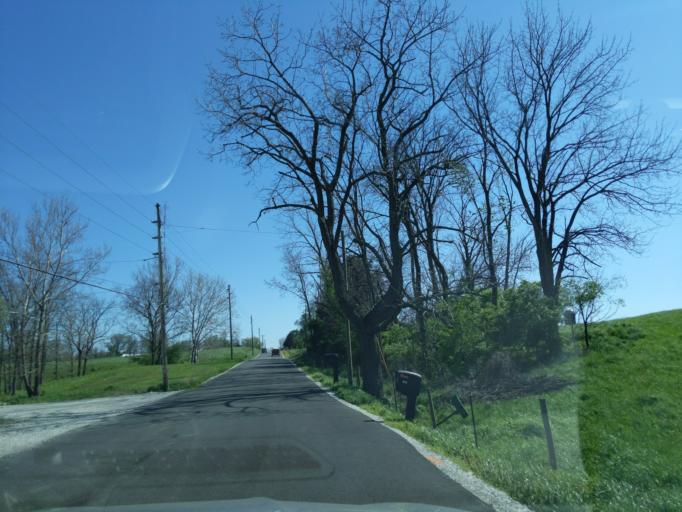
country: US
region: Indiana
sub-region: Decatur County
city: Greensburg
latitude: 39.3241
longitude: -85.4888
